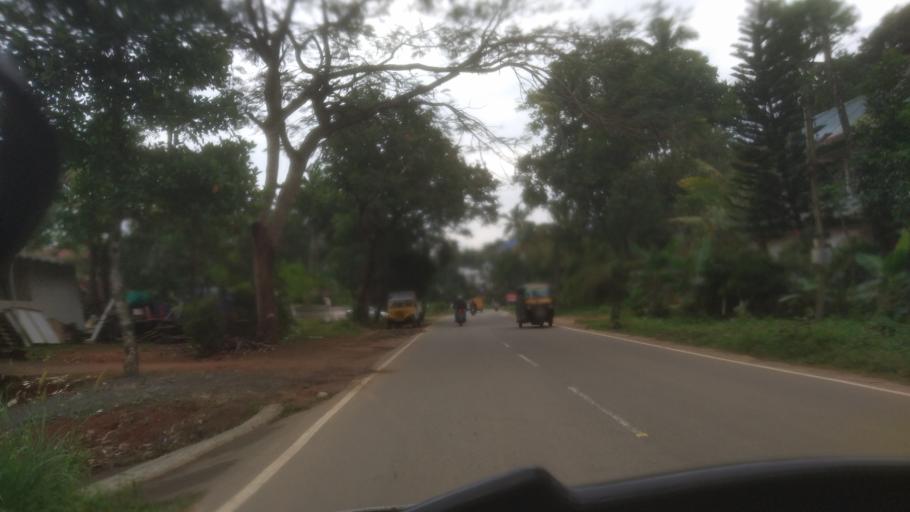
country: IN
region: Kerala
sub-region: Idukki
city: Munnar
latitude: 9.9973
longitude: 76.9736
